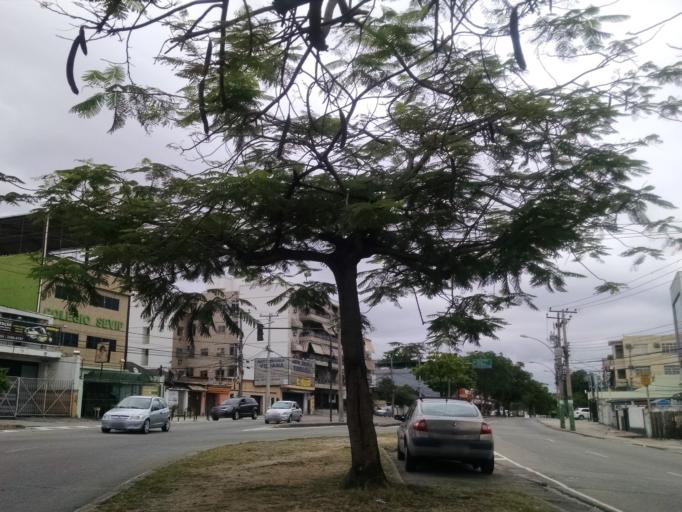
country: BR
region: Rio de Janeiro
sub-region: Duque De Caxias
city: Duque de Caxias
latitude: -22.8366
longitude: -43.3091
